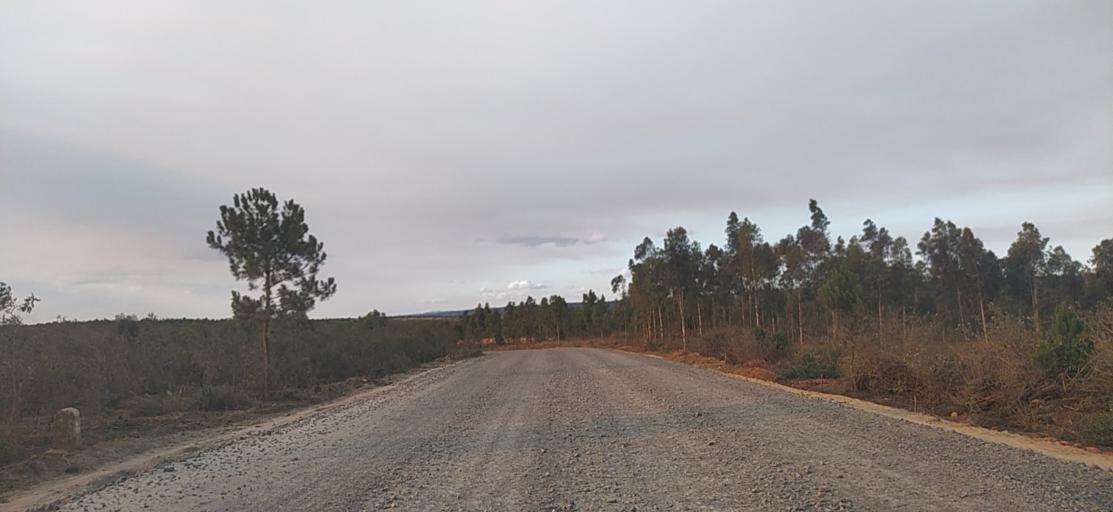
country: MG
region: Analamanga
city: Anjozorobe
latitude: -18.5036
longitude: 48.2676
